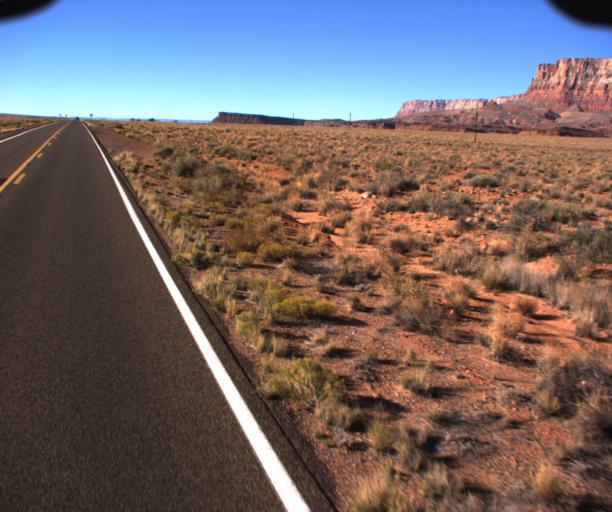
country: US
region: Arizona
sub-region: Coconino County
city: Page
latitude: 36.7986
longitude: -111.6786
